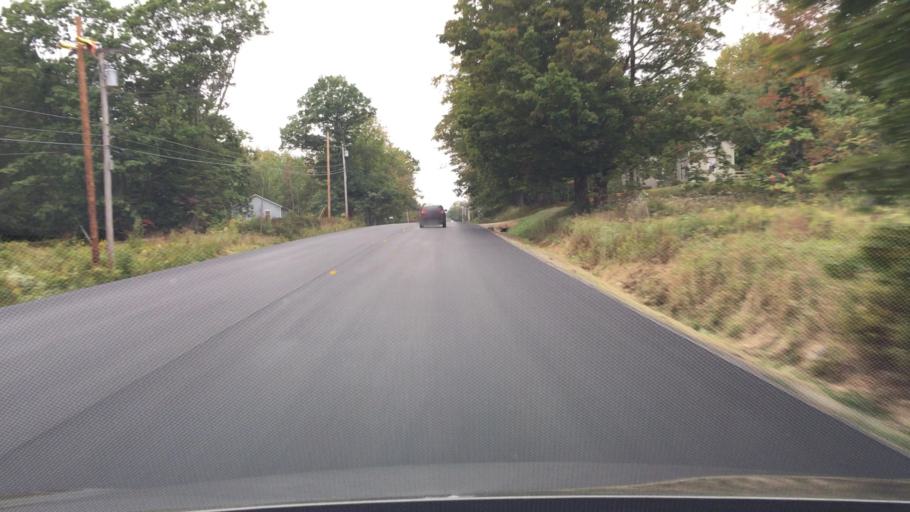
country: US
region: Maine
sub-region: Waldo County
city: Belfast
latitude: 44.4123
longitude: -69.0663
